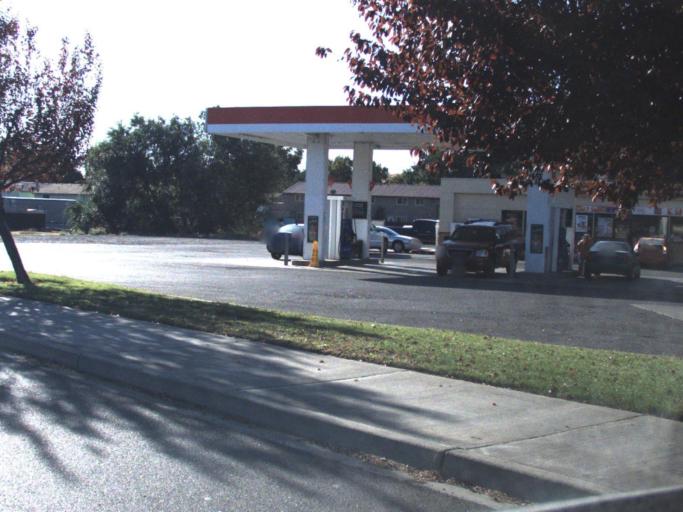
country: US
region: Washington
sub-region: Benton County
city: West Richland
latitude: 46.2972
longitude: -119.3391
